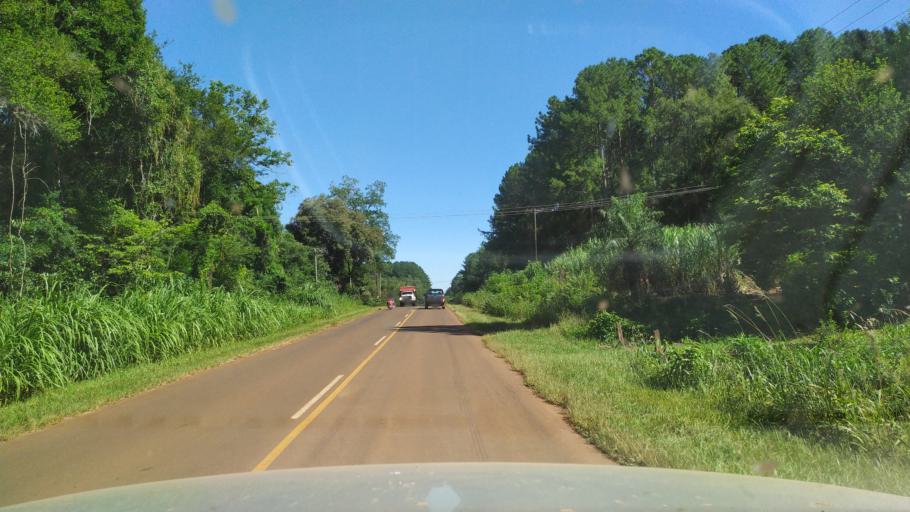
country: AR
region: Misiones
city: Caraguatay
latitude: -26.6667
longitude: -54.7296
